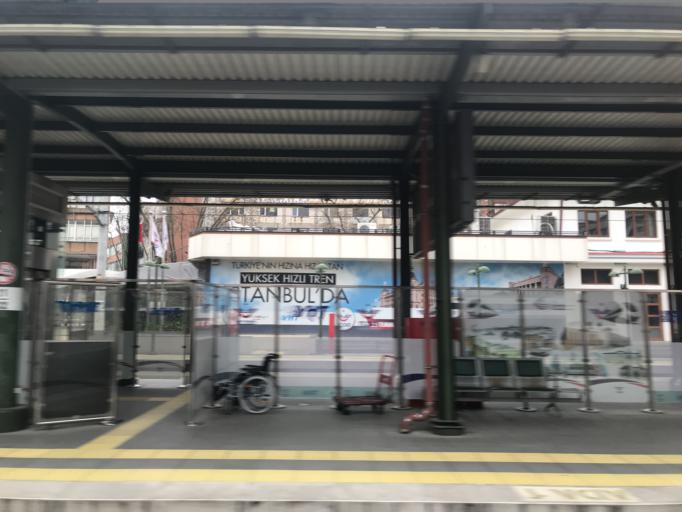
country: TR
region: Istanbul
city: Pendik
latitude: 40.8803
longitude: 29.2315
